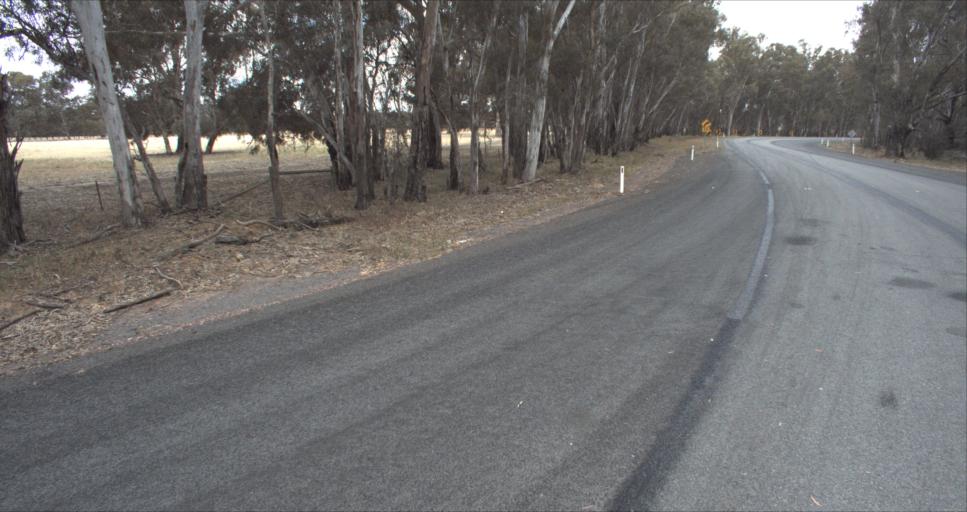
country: AU
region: New South Wales
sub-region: Leeton
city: Leeton
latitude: -34.6323
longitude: 146.3746
